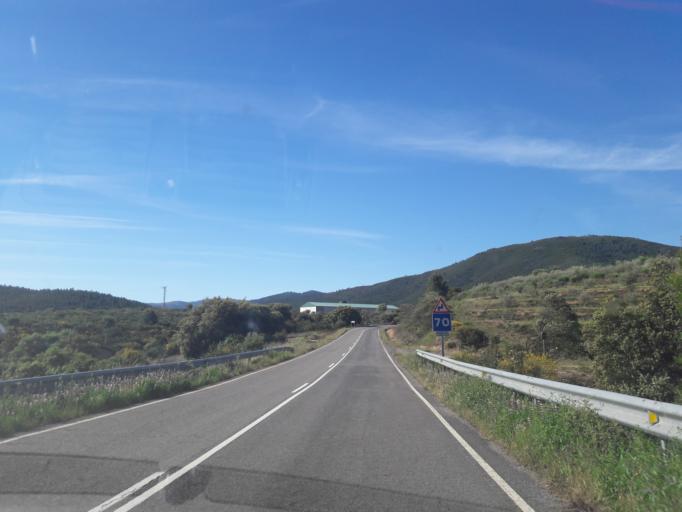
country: ES
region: Castille and Leon
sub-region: Provincia de Salamanca
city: Sotoserrano
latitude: 40.4185
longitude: -6.0352
